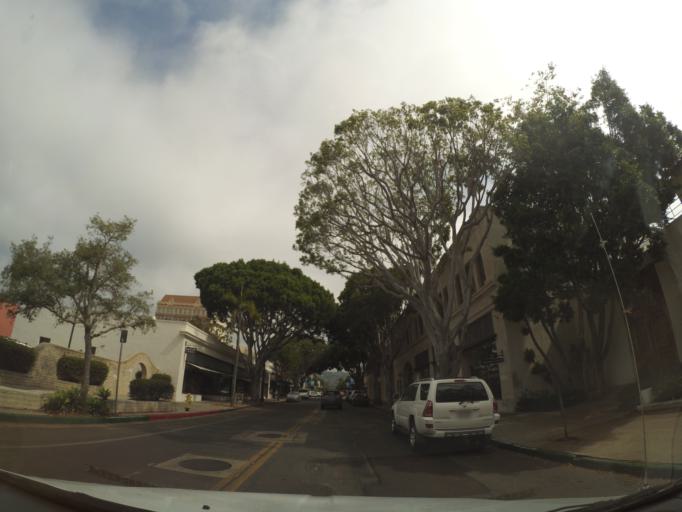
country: US
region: California
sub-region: Santa Barbara County
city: Santa Barbara
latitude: 34.4227
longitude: -119.7052
